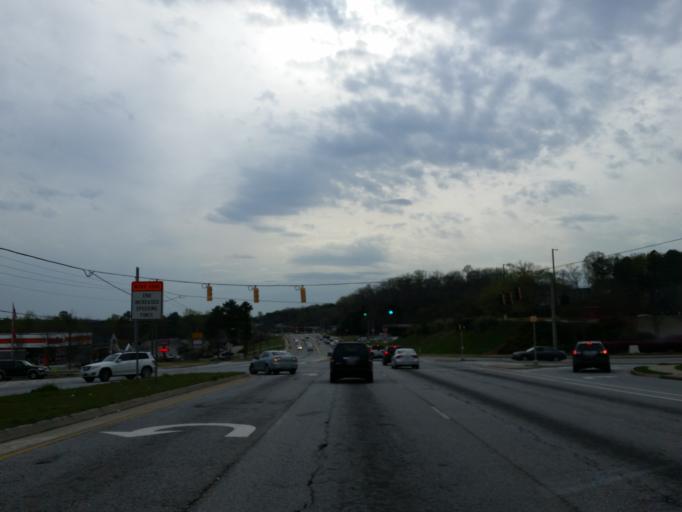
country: US
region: Georgia
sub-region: Henry County
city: Stockbridge
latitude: 33.5046
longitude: -84.2354
